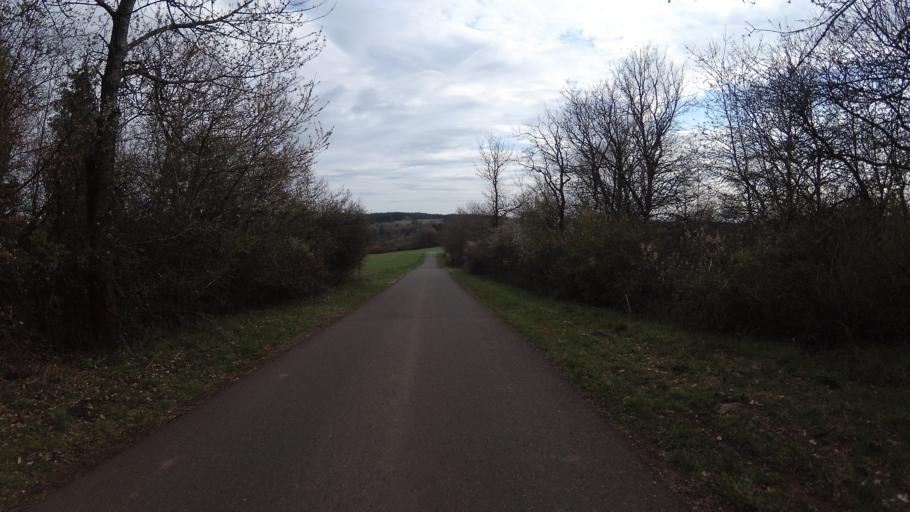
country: DE
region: Rheinland-Pfalz
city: Hahnweiler
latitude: 49.5622
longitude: 7.2137
